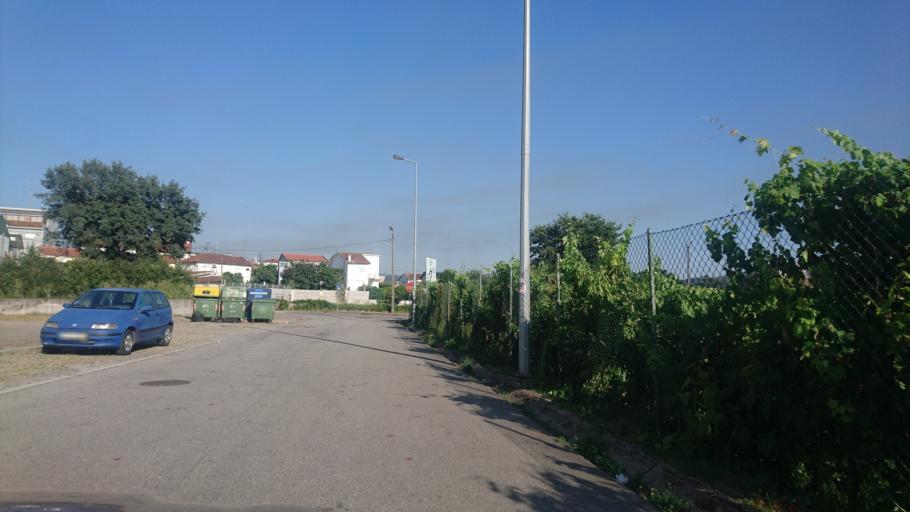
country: PT
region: Porto
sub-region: Paredes
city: Recarei
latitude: 41.1529
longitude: -8.4046
